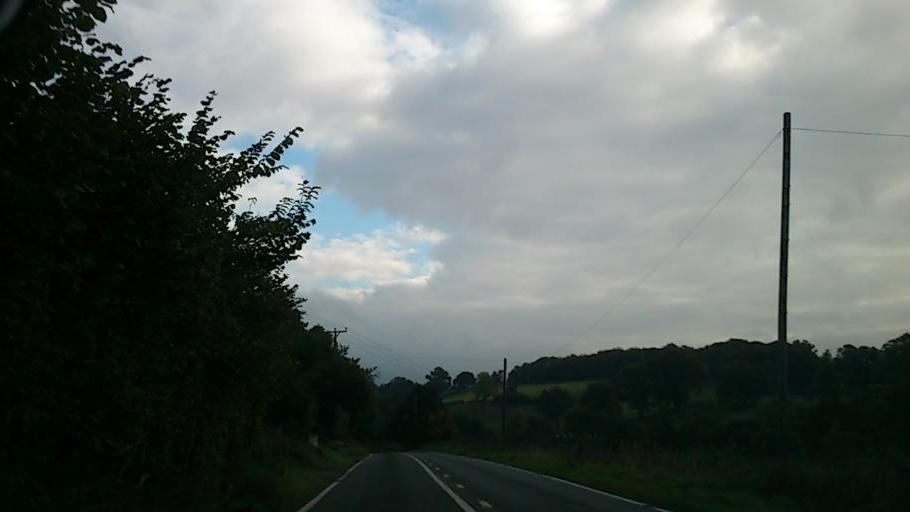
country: GB
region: Wales
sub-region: Sir Powys
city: Welshpool
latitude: 52.6561
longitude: -3.1710
